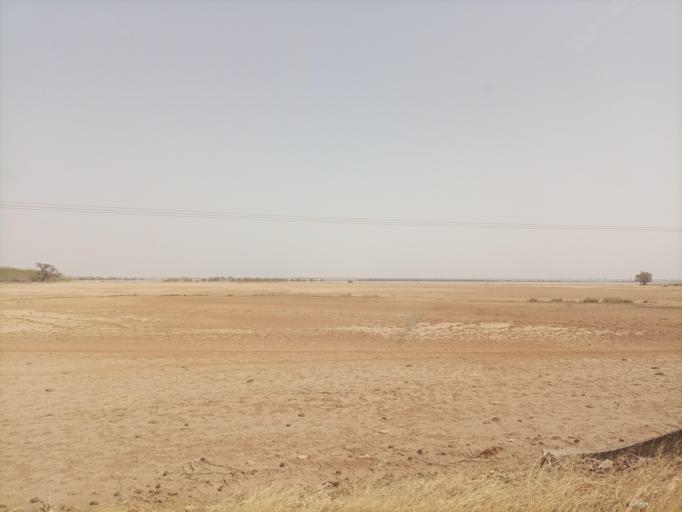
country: SN
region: Fatick
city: Foundiougne
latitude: 14.1756
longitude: -16.4589
